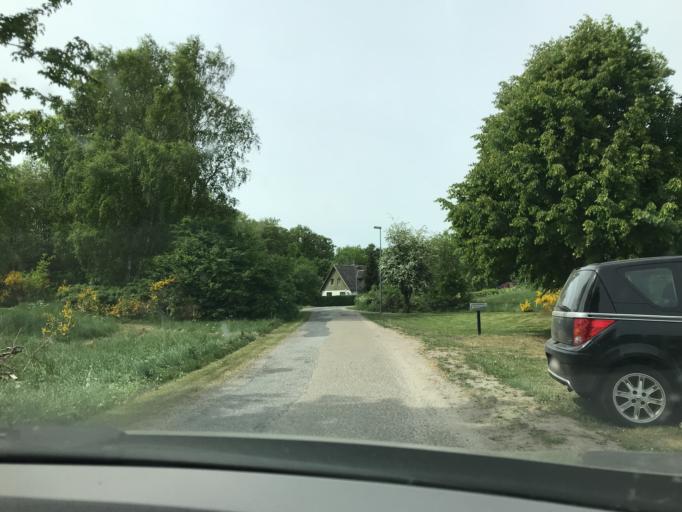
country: DK
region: Central Jutland
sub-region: Norddjurs Kommune
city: Allingabro
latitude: 56.5984
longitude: 10.3132
